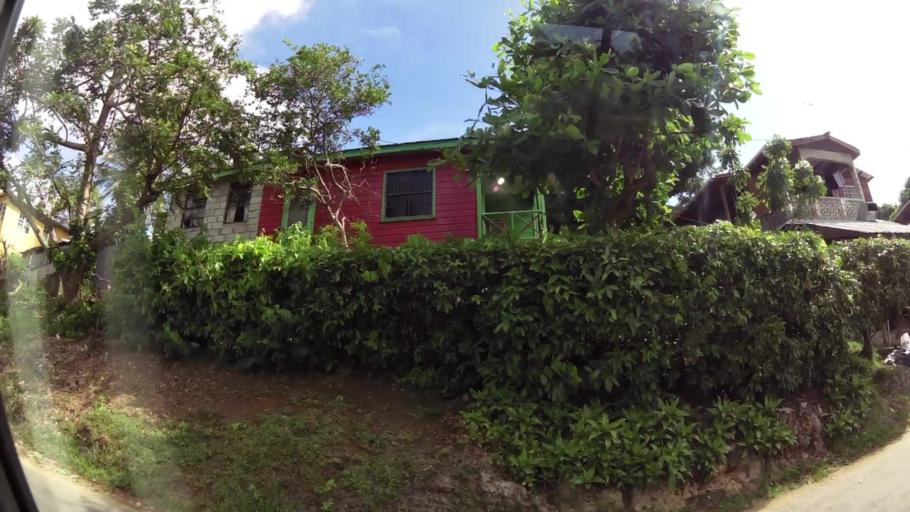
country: BB
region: Saint James
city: Holetown
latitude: 13.2119
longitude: -59.6058
